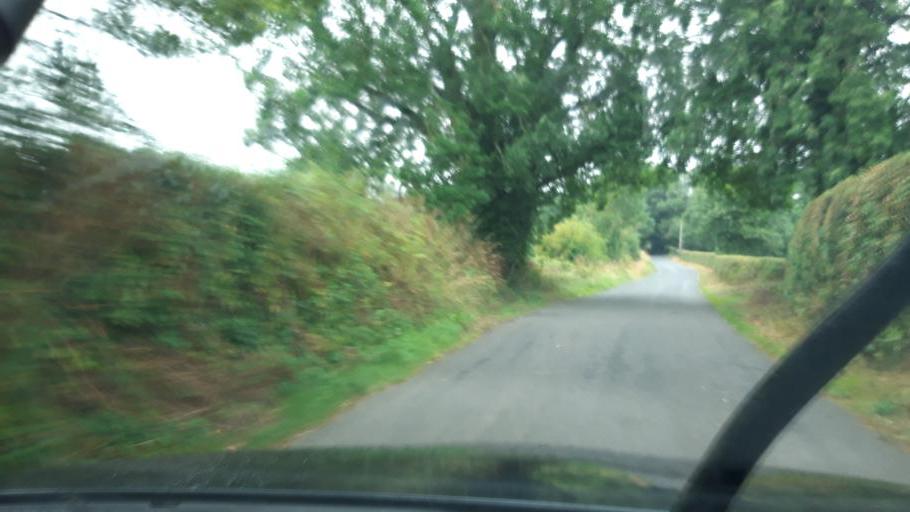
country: IE
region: Leinster
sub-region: Kilkenny
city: Callan
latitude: 52.6579
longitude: -7.4355
